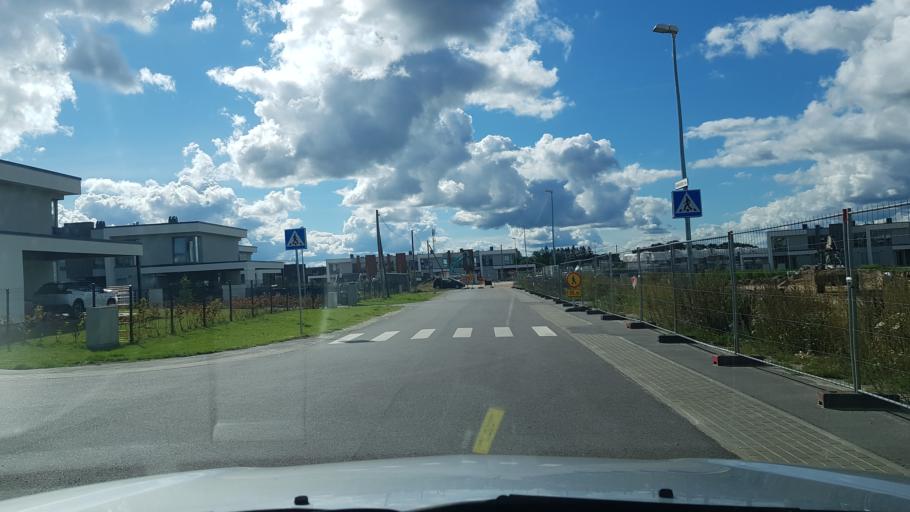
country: EE
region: Harju
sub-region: Tallinna linn
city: Tallinn
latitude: 59.3860
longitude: 24.8027
